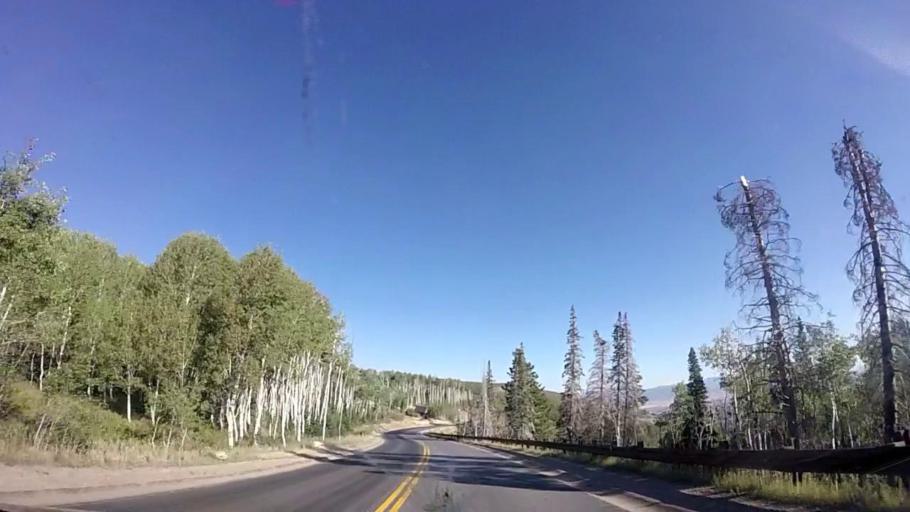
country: US
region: Utah
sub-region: Summit County
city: Park City
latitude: 40.6221
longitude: -111.4978
